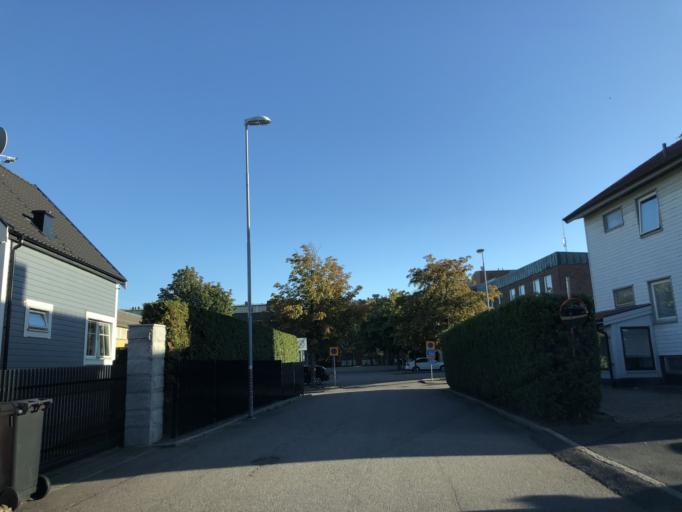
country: SE
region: Vaestra Goetaland
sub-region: Molndal
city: Moelndal
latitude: 57.6627
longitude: 12.0102
